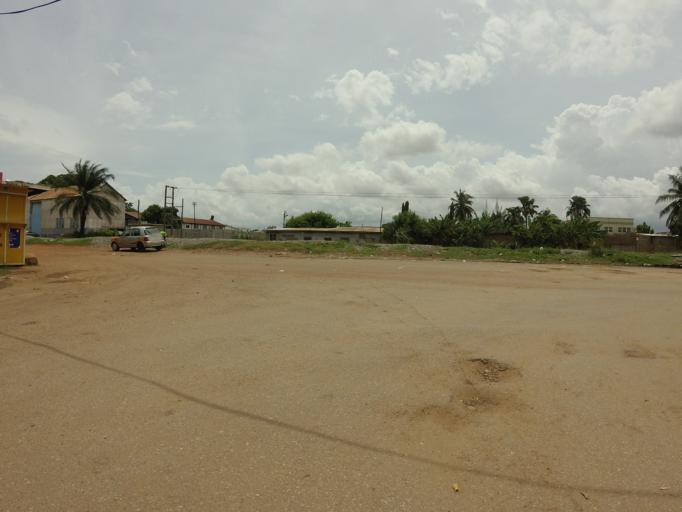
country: GH
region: Greater Accra
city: Accra
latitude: 5.6044
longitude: -0.2105
